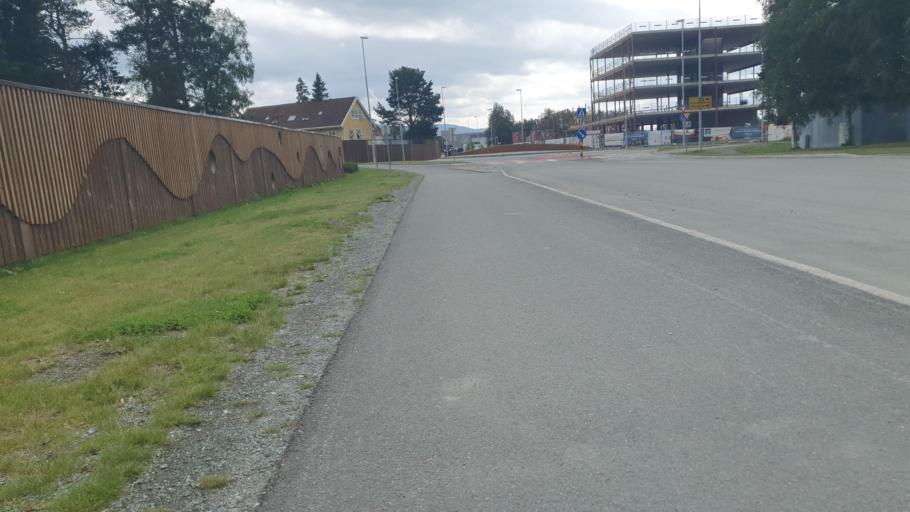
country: NO
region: Sor-Trondelag
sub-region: Trondheim
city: Trondheim
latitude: 63.3493
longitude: 10.3601
